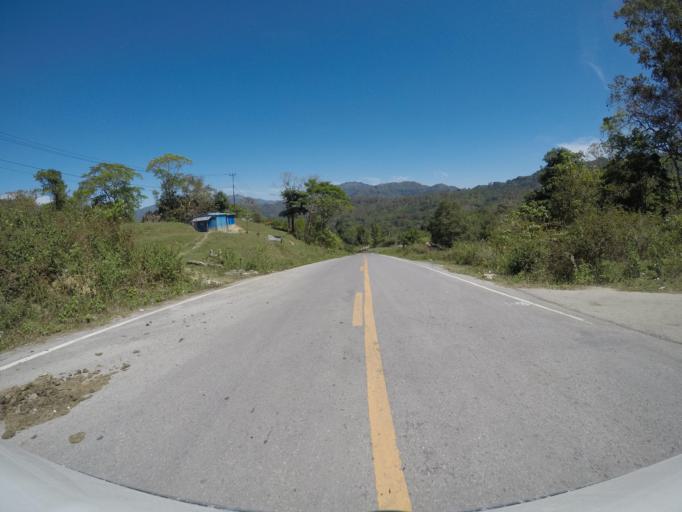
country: TL
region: Manatuto
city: Manatuto
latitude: -8.8255
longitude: 125.9817
